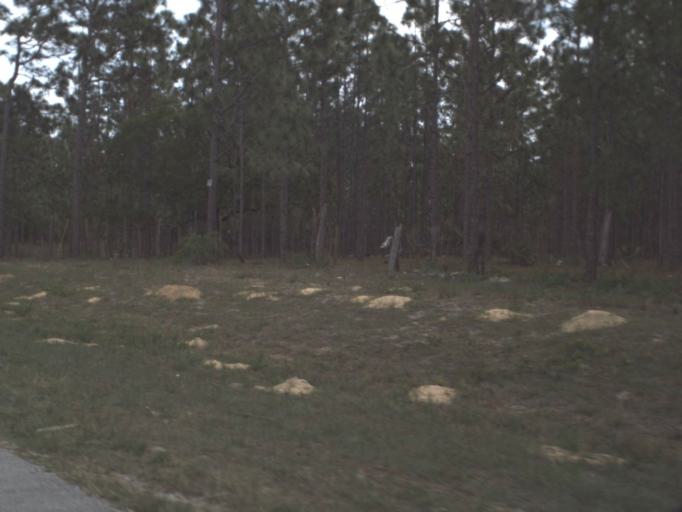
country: US
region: Florida
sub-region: Lake County
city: Mount Plymouth
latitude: 28.8536
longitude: -81.5240
